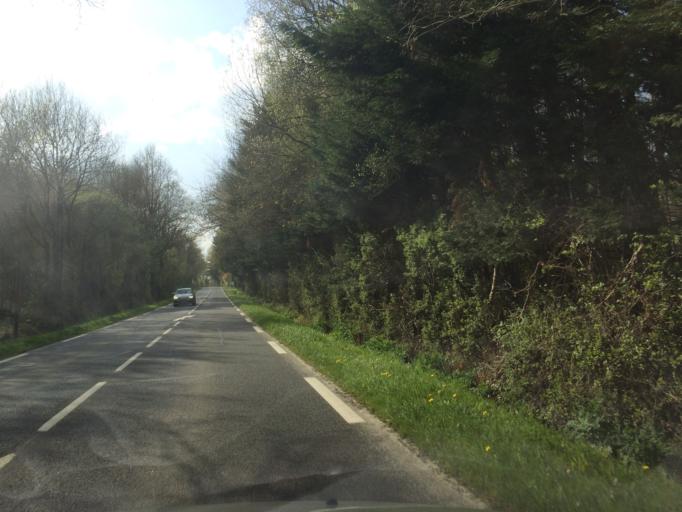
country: FR
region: Pays de la Loire
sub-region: Departement de la Loire-Atlantique
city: Blain
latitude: 47.4846
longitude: -1.8195
